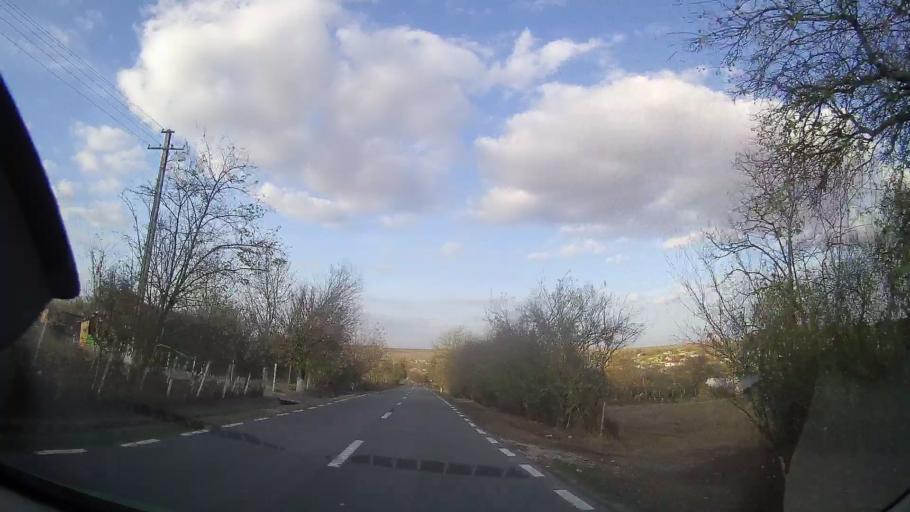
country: RO
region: Constanta
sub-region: Comuna Independenta
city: Independenta
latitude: 43.9516
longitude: 28.0750
